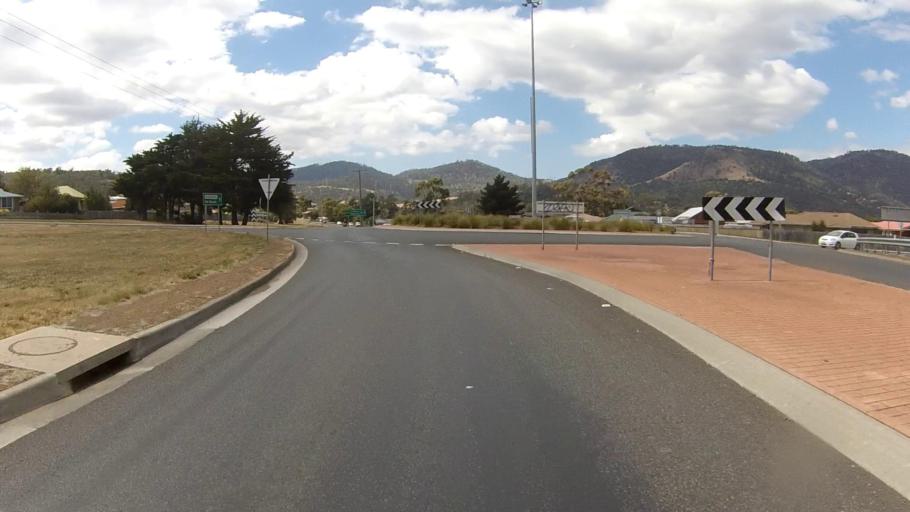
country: AU
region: Tasmania
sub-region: Brighton
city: Old Beach
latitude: -42.7783
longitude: 147.2761
